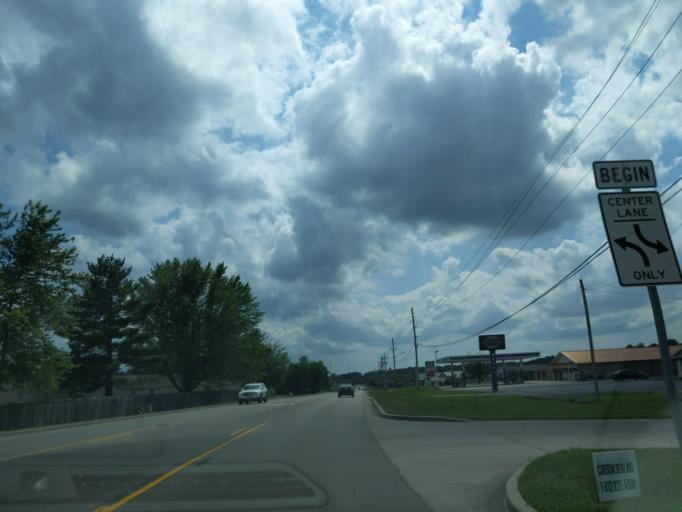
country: US
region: Indiana
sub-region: Ripley County
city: Batesville
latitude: 39.3132
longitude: -85.2092
